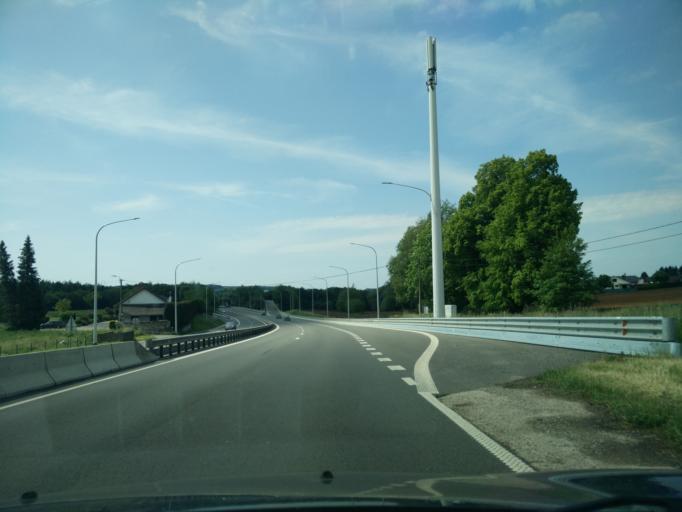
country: BE
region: Wallonia
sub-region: Province de Namur
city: Walcourt
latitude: 50.2922
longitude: 4.4806
